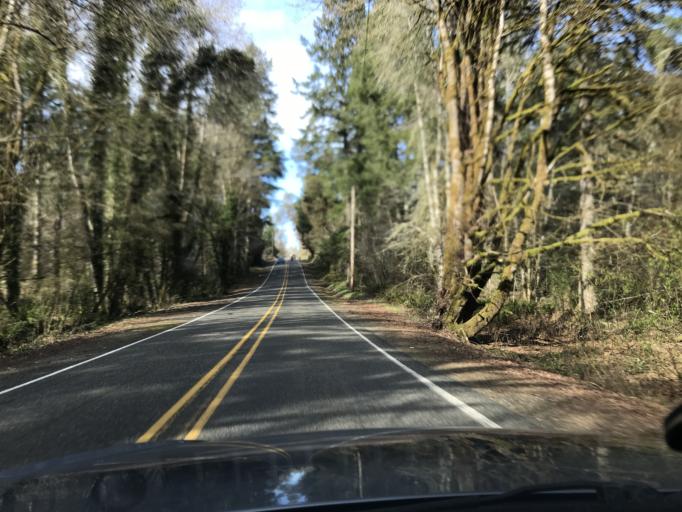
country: US
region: Washington
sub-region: Pierce County
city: Longbranch
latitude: 47.2254
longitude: -122.7908
